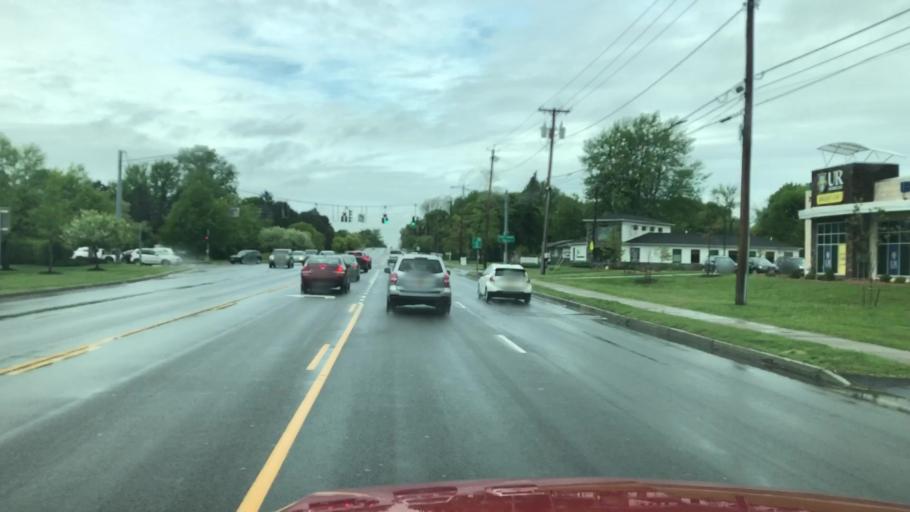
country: US
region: New York
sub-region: Monroe County
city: Fairport
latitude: 43.1309
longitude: -77.4458
